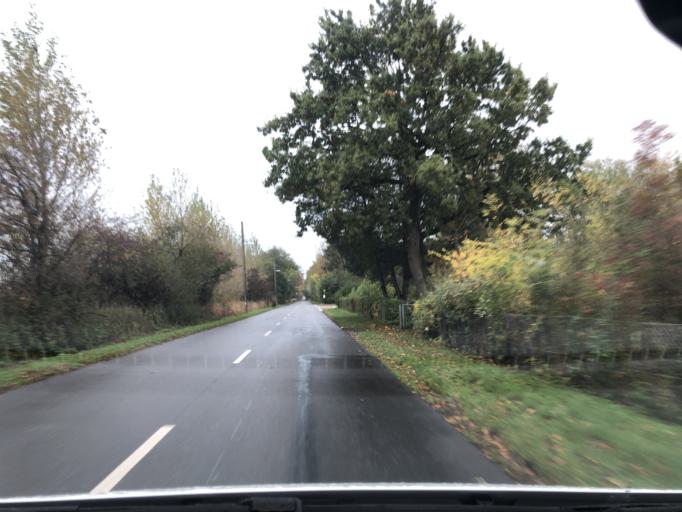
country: DK
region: Capital Region
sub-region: Tarnby Kommune
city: Tarnby
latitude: 55.5653
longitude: 12.5859
